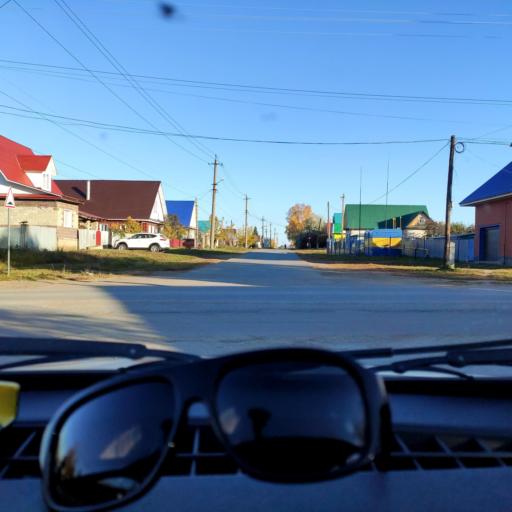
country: RU
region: Bashkortostan
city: Blagoveshchensk
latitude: 55.0268
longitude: 55.9895
